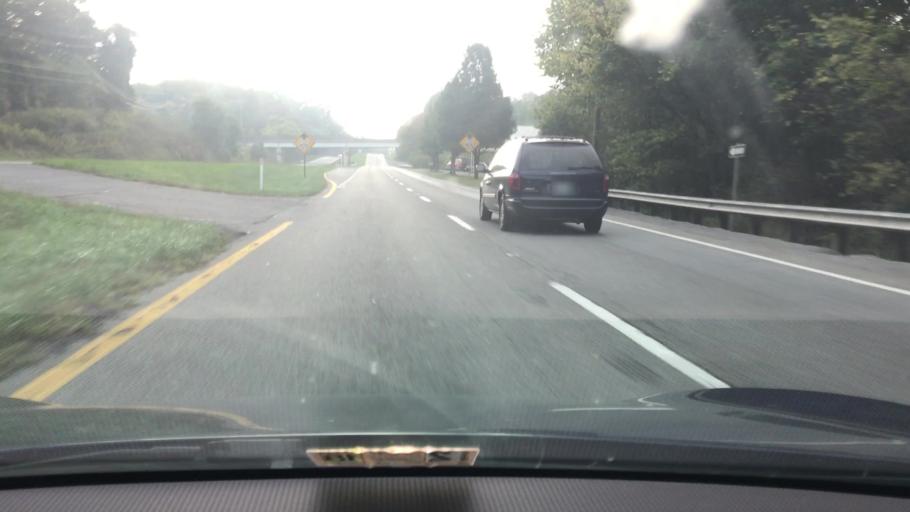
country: US
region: Virginia
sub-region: Botetourt County
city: Blue Ridge
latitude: 37.3960
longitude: -79.7494
